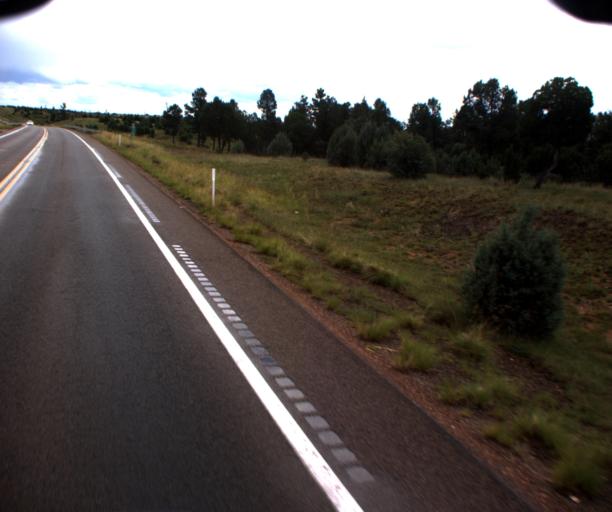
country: US
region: Arizona
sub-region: Navajo County
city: Heber-Overgaard
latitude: 34.3818
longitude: -110.4872
